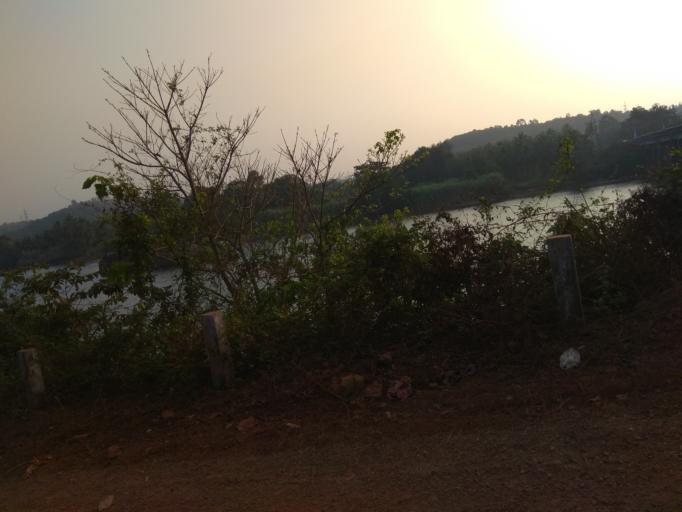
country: IN
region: Karnataka
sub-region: Dakshina Kannada
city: Mangalore
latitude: 12.9415
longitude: 74.8668
